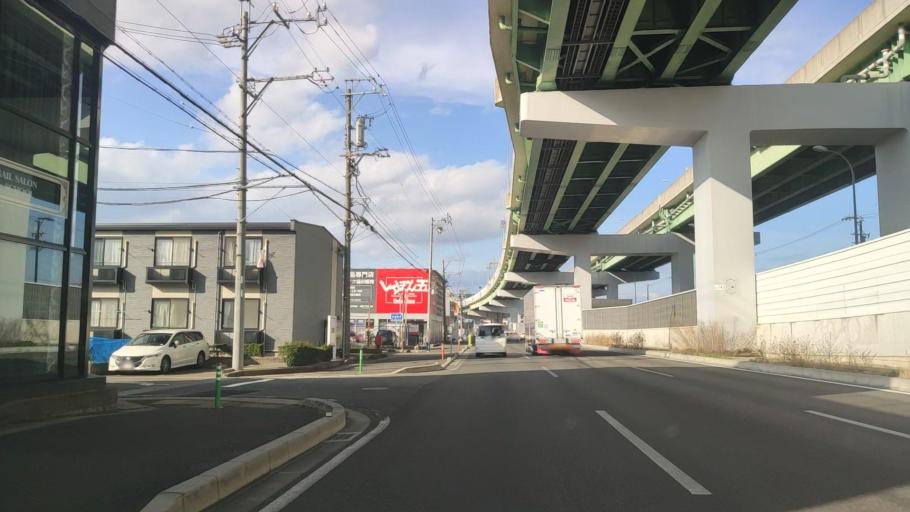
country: JP
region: Aichi
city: Ichinomiya
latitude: 35.2835
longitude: 136.8298
